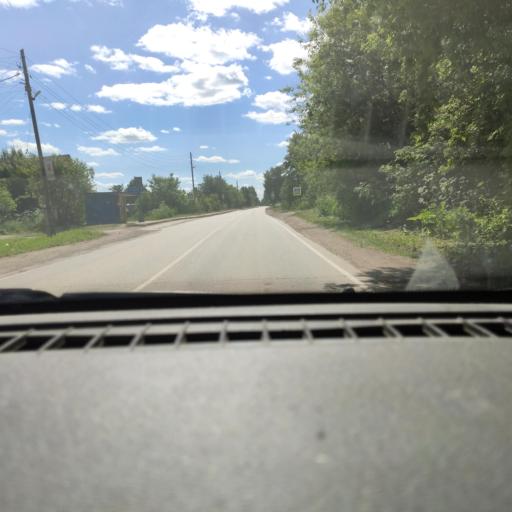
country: RU
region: Perm
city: Chaykovskaya
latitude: 58.1091
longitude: 55.5807
